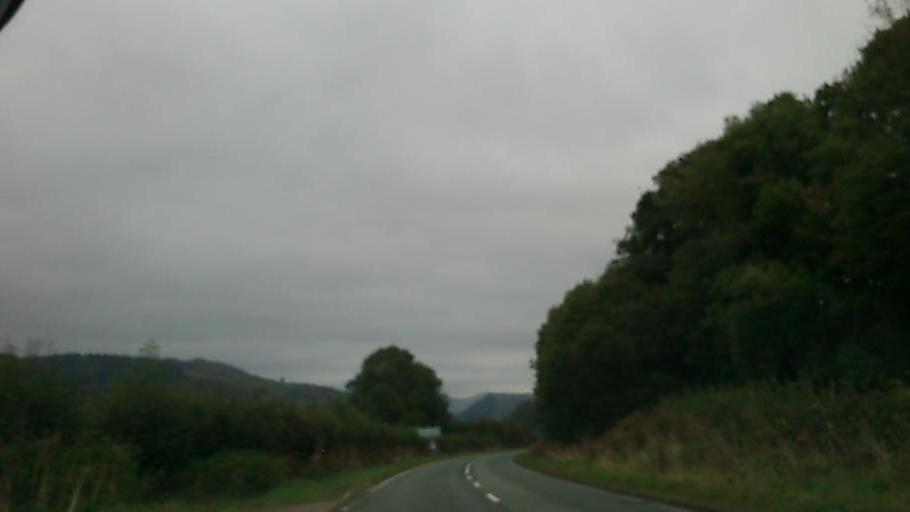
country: GB
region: Wales
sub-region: Gwynedd
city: Corris
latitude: 52.6694
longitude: -3.7068
